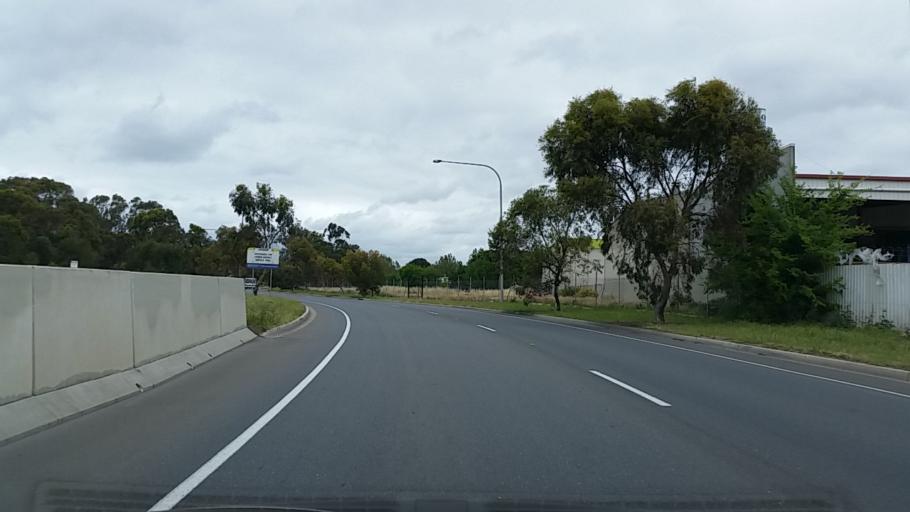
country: AU
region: South Australia
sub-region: Prospect
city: Prospect
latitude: -34.8681
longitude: 138.5749
